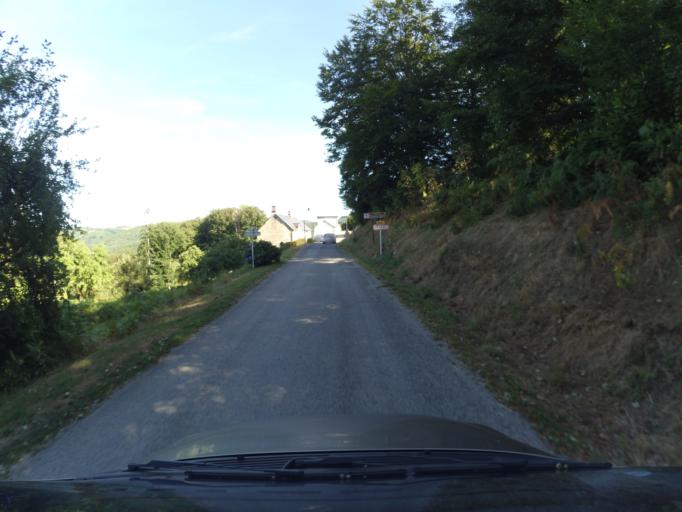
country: FR
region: Limousin
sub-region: Departement de la Correze
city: Bugeat
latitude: 45.6887
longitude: 1.8889
